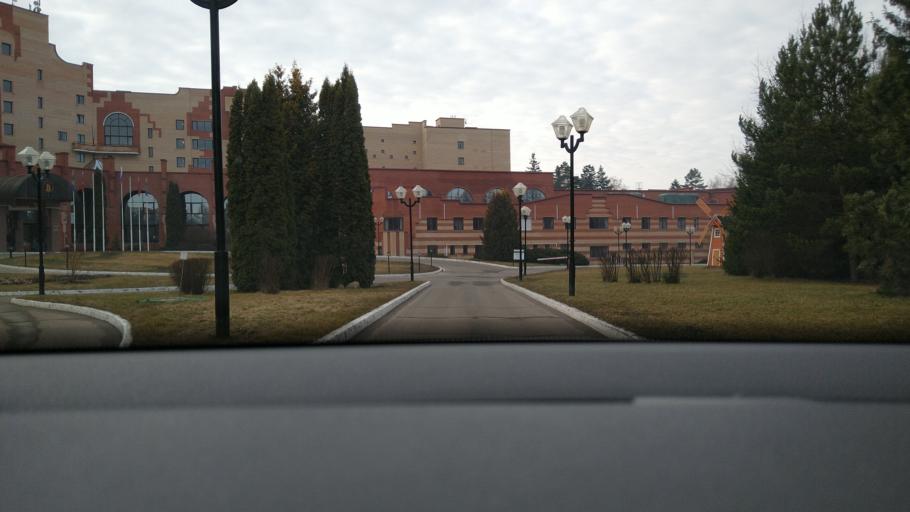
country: RU
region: Moskovskaya
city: Vatutinki
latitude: 55.5149
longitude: 37.3348
